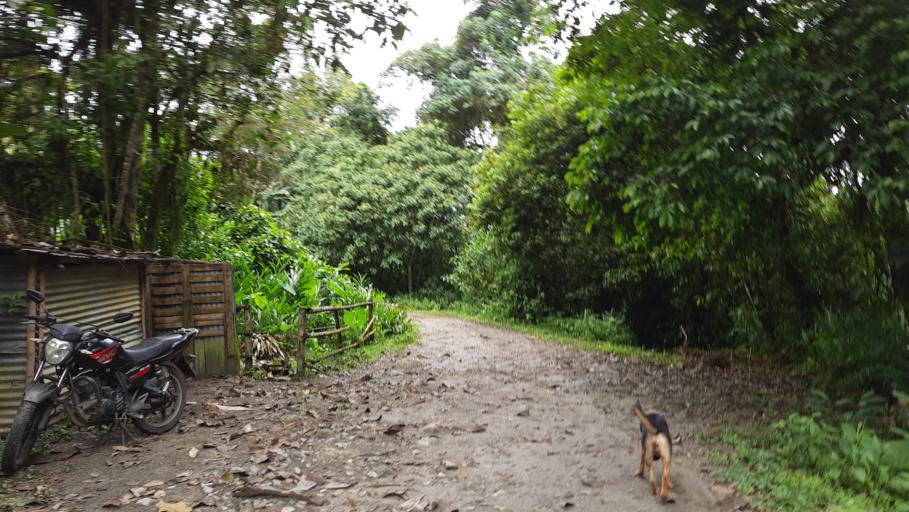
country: CO
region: Valle del Cauca
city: Buga
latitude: 3.8546
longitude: -76.1880
